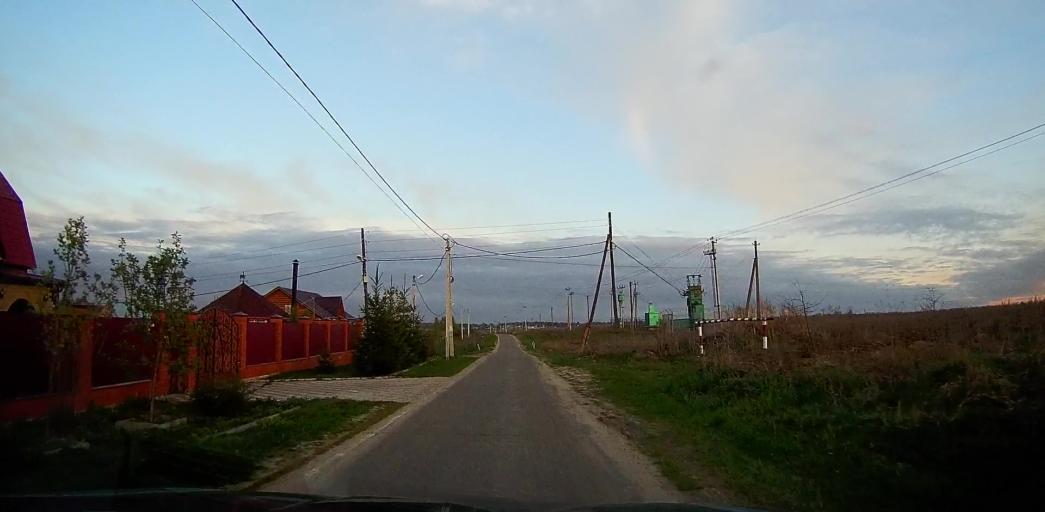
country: RU
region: Moskovskaya
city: Peski
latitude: 55.2285
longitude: 38.7339
